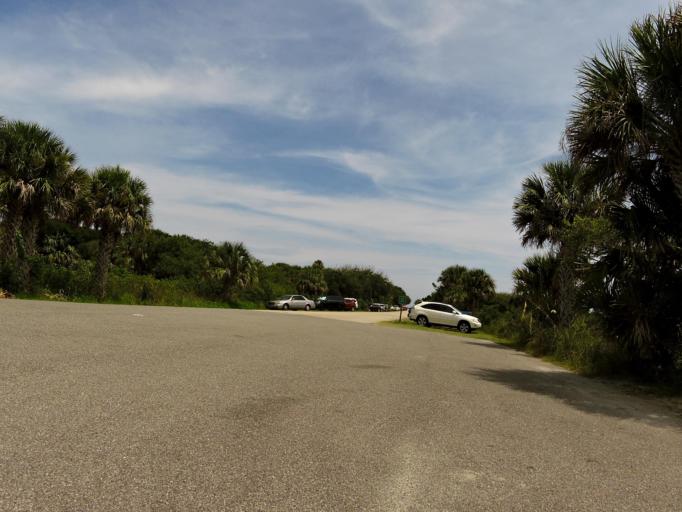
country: US
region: Florida
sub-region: Volusia County
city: Ponce Inlet
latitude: 29.0790
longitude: -80.9251
